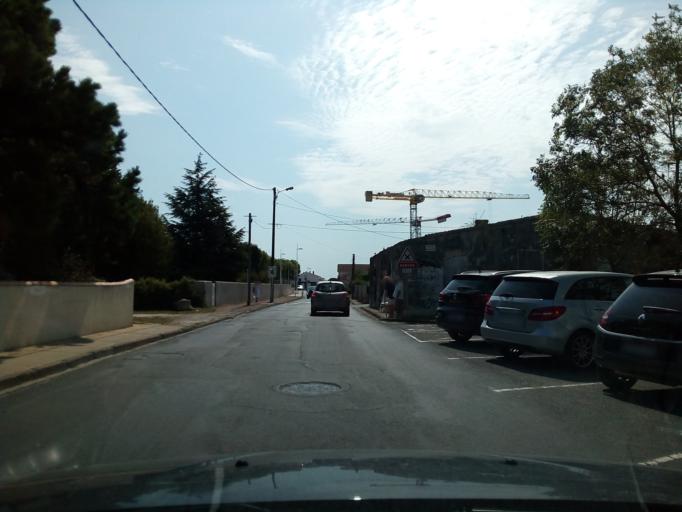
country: FR
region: Poitou-Charentes
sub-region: Departement de la Charente-Maritime
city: Dolus-d'Oleron
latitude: 45.9416
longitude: -1.3097
